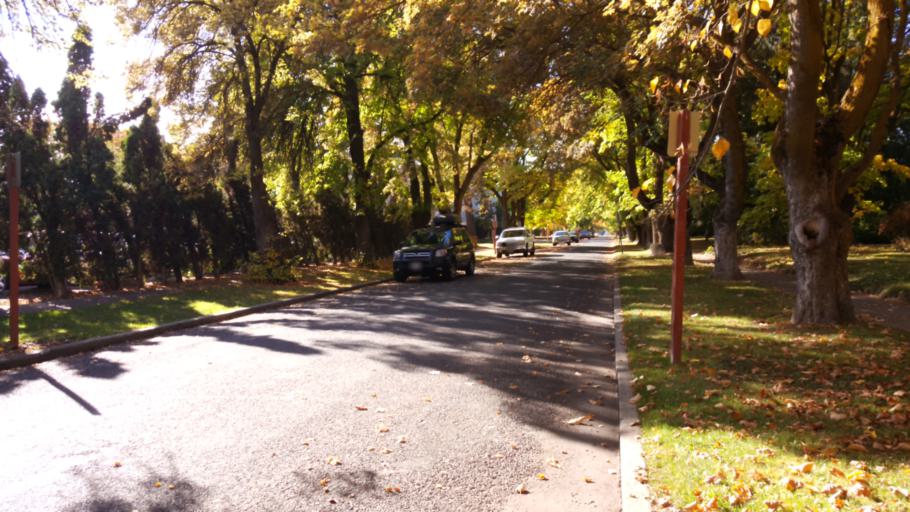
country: US
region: Washington
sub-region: Kittitas County
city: Ellensburg
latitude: 47.0008
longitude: -120.5434
